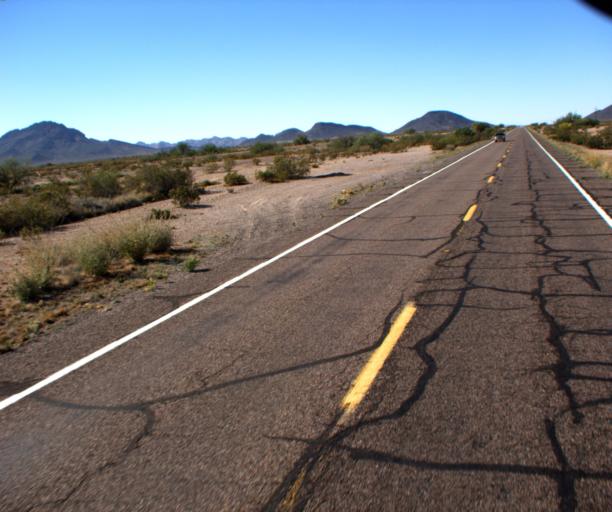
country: US
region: Arizona
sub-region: Maricopa County
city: Gila Bend
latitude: 32.8042
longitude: -112.7973
